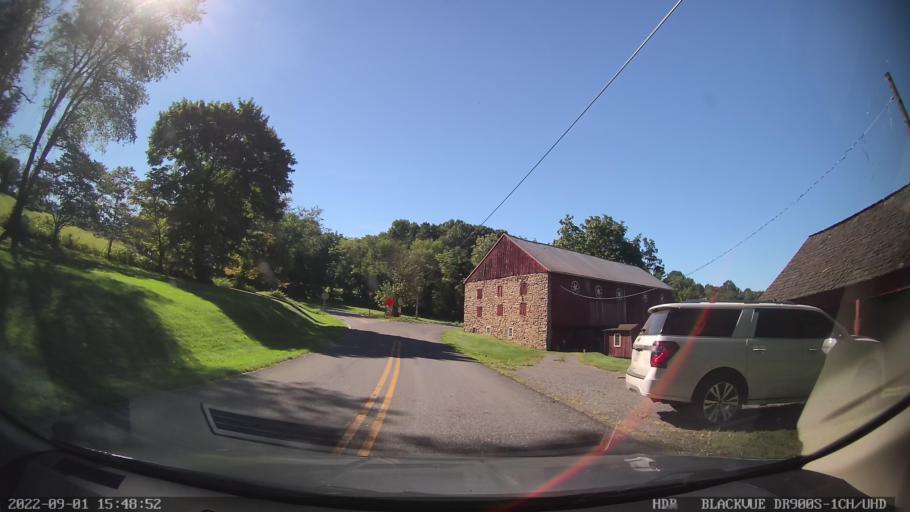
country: US
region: Pennsylvania
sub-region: Berks County
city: Topton
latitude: 40.4703
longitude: -75.7322
